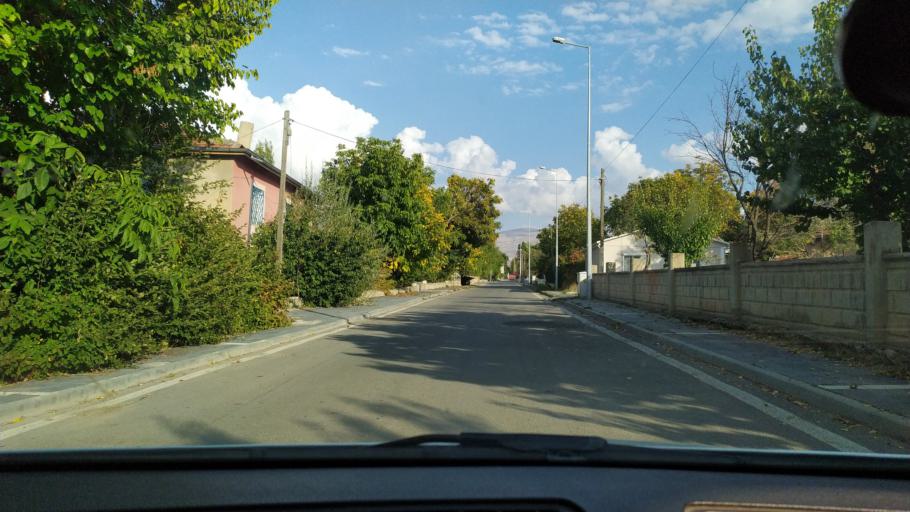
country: TR
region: Kayseri
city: Akkisla
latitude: 38.9998
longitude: 36.1661
